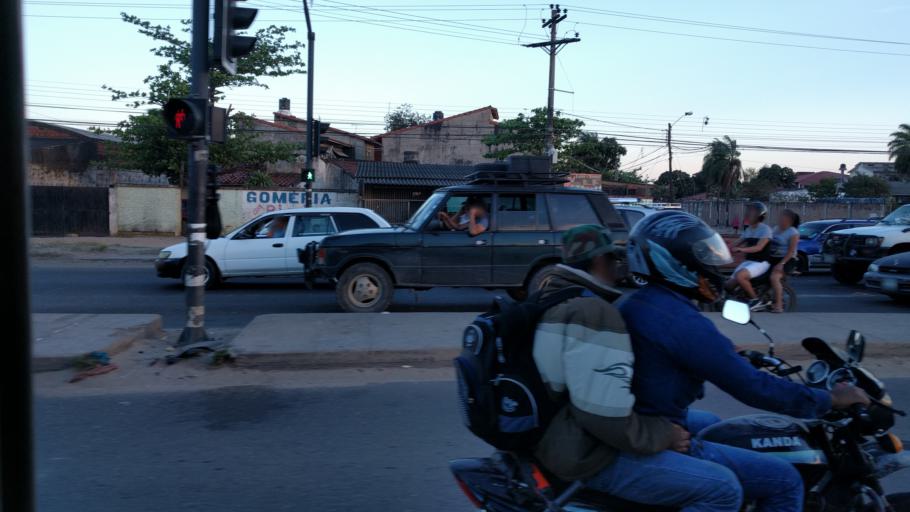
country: BO
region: Santa Cruz
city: Santa Cruz de la Sierra
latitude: -17.7677
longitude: -63.1150
